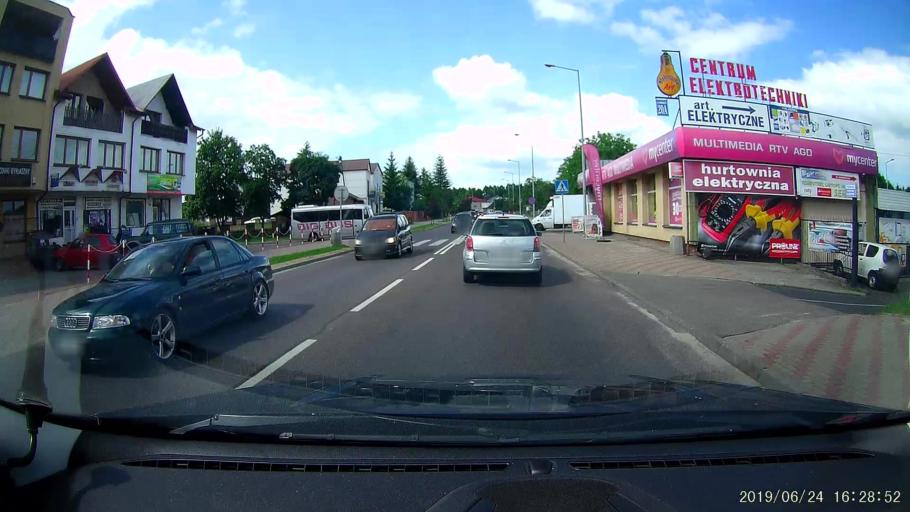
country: PL
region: Lublin Voivodeship
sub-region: Powiat tomaszowski
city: Tomaszow Lubelski
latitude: 50.4558
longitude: 23.4205
